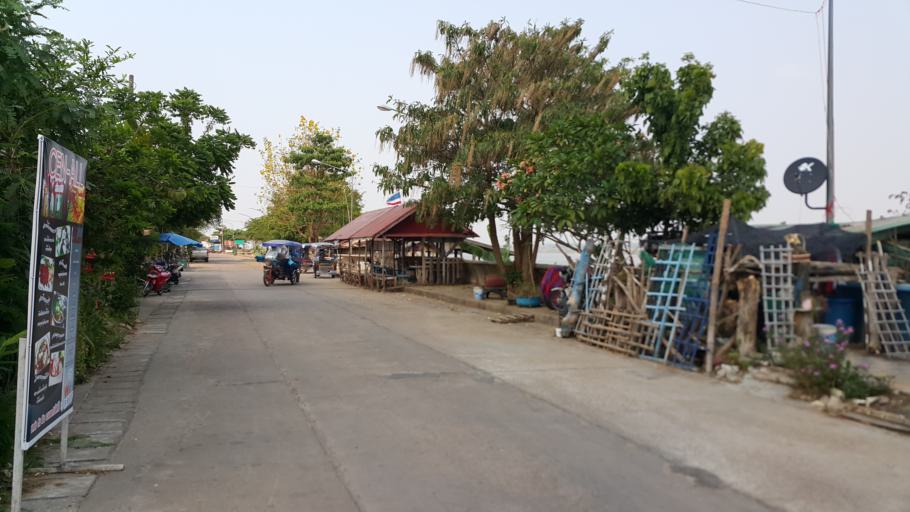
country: TH
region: Nakhon Phanom
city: That Phanom
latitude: 16.9405
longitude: 104.7291
